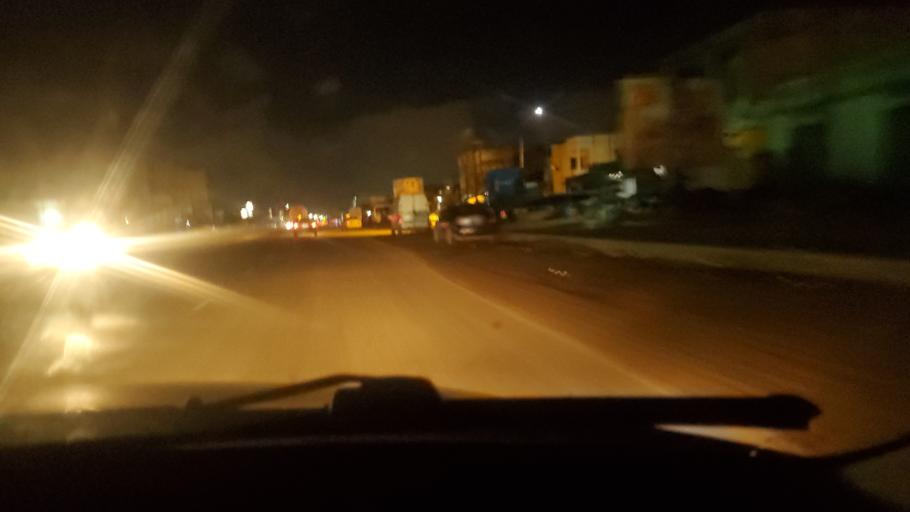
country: SN
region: Dakar
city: Pikine
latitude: 14.7444
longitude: -17.3843
